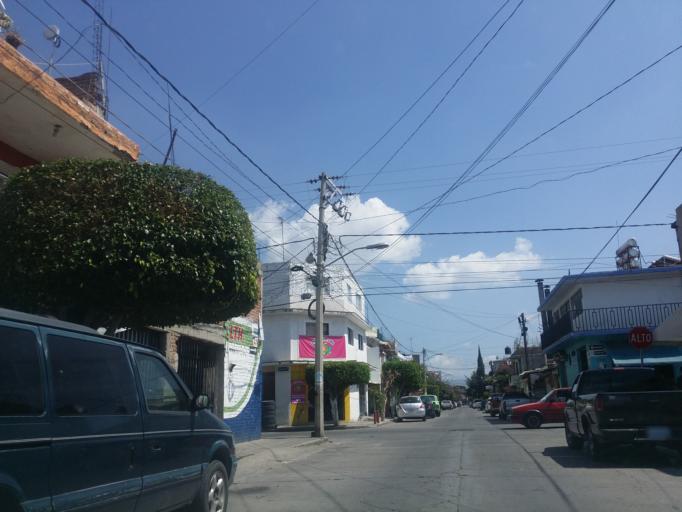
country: MX
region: Guanajuato
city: Leon
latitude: 21.1431
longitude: -101.6704
